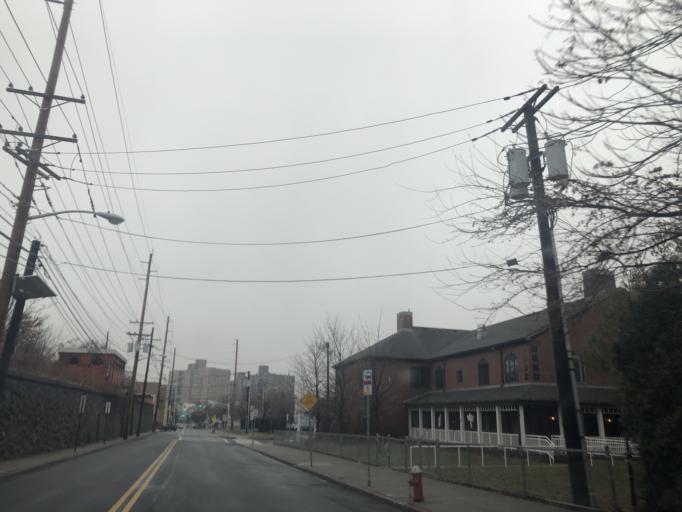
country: US
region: New Jersey
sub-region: Hudson County
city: Jersey City
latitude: 40.7395
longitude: -74.0563
